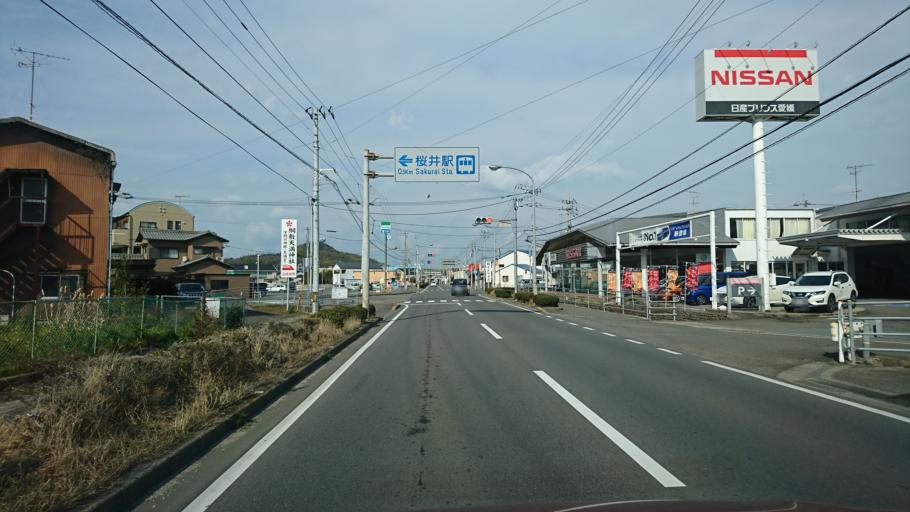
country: JP
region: Ehime
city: Saijo
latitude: 34.0150
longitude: 133.0384
